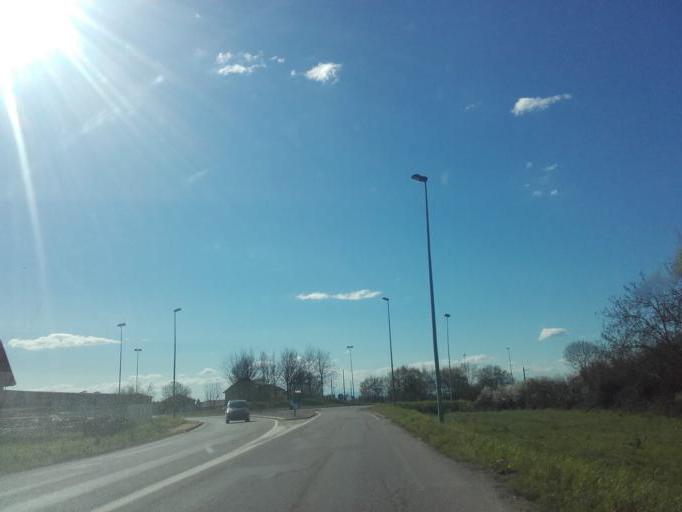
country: FR
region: Rhone-Alpes
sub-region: Departement de l'Isere
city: Saint-Etienne-de-Saint-Geoirs
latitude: 45.3479
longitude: 5.3398
